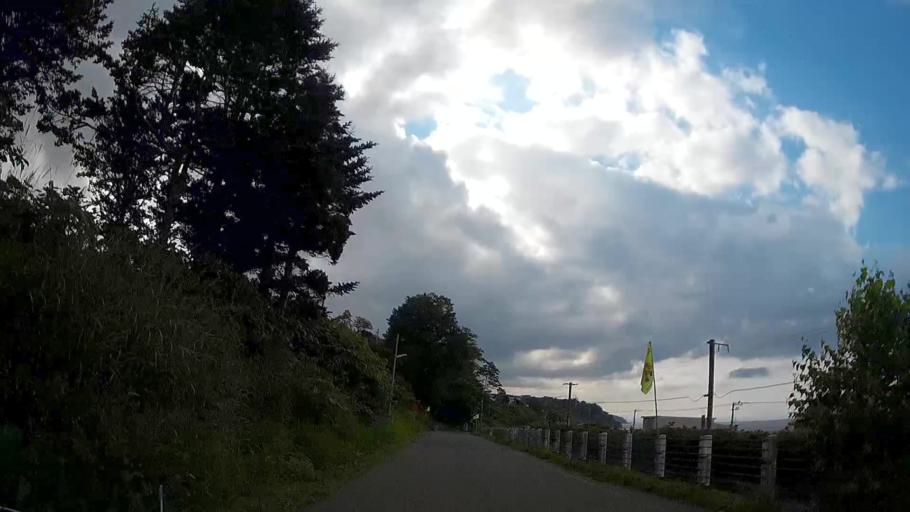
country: JP
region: Hokkaido
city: Nanae
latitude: 42.1134
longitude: 140.5472
